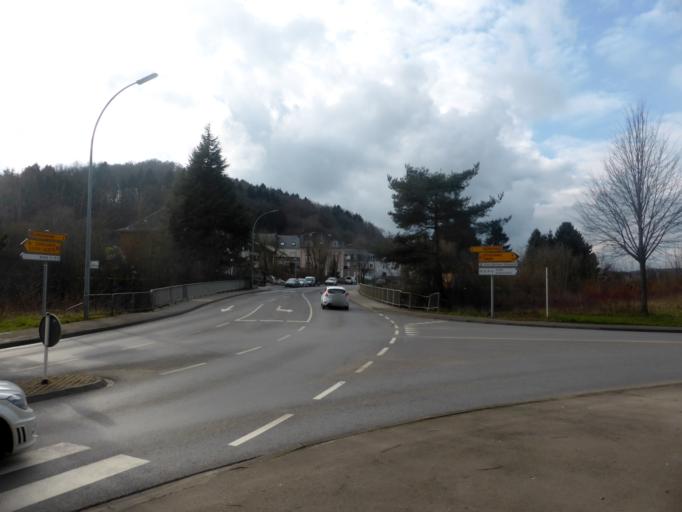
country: LU
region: Luxembourg
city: Belvaux
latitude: 49.5141
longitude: 5.9300
